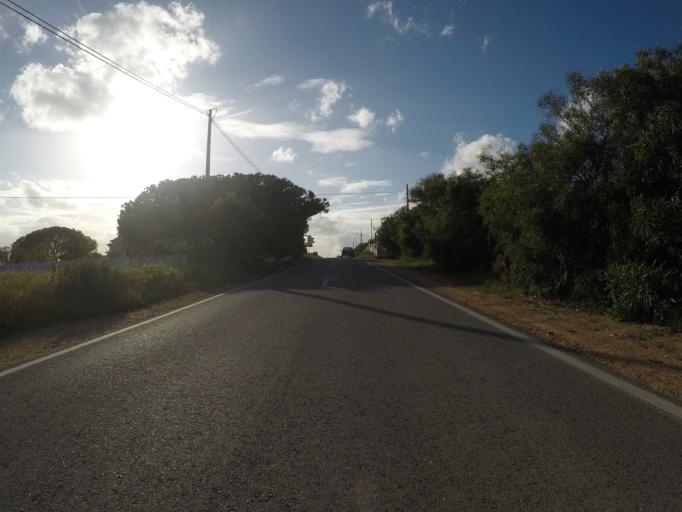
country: PT
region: Faro
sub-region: Lagoa
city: Carvoeiro
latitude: 37.0969
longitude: -8.4394
